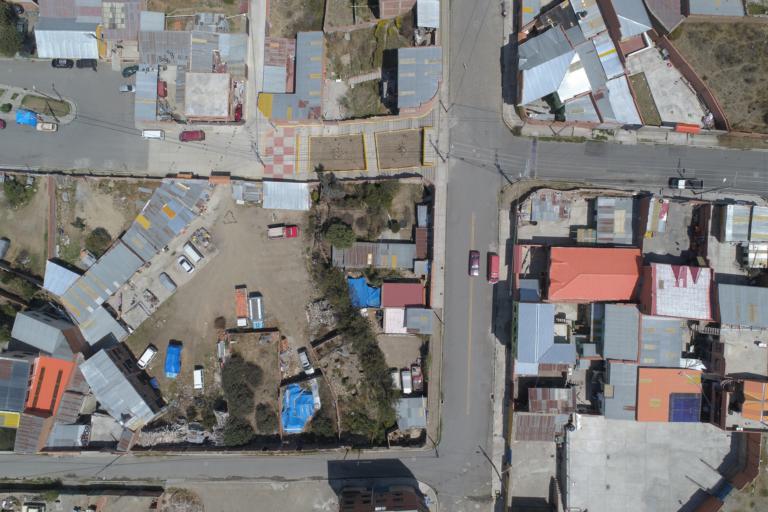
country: BO
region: La Paz
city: La Paz
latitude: -16.5043
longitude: -68.1014
